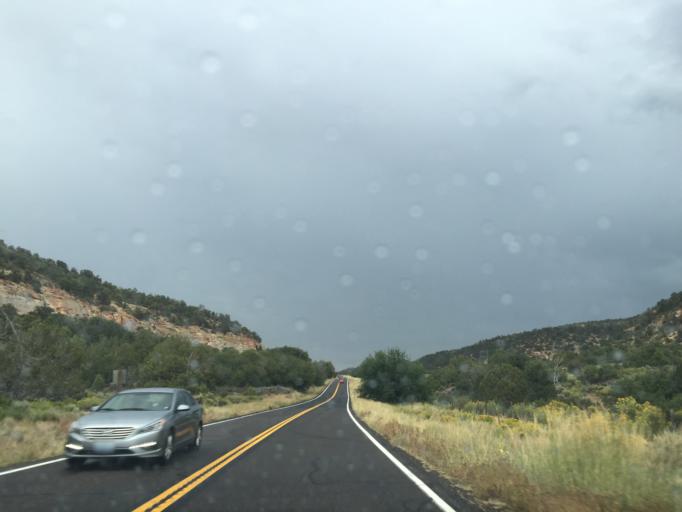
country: US
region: Utah
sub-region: Washington County
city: Hildale
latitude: 37.2379
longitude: -112.8499
